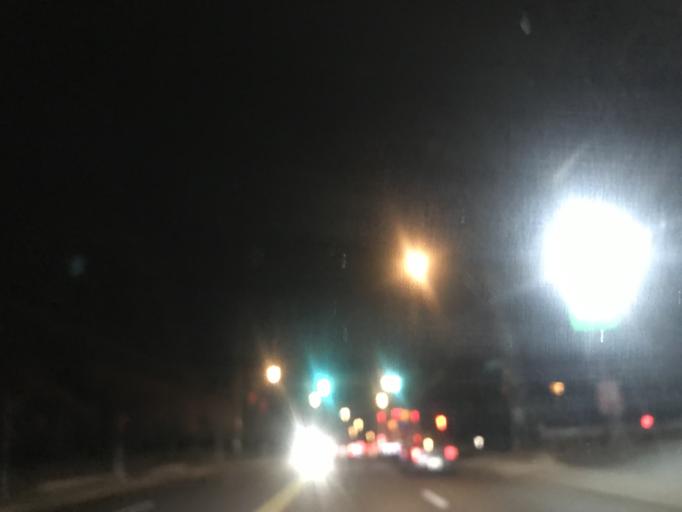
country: US
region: Maryland
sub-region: Prince George's County
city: Oxon Hill
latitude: 38.8048
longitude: -76.9742
